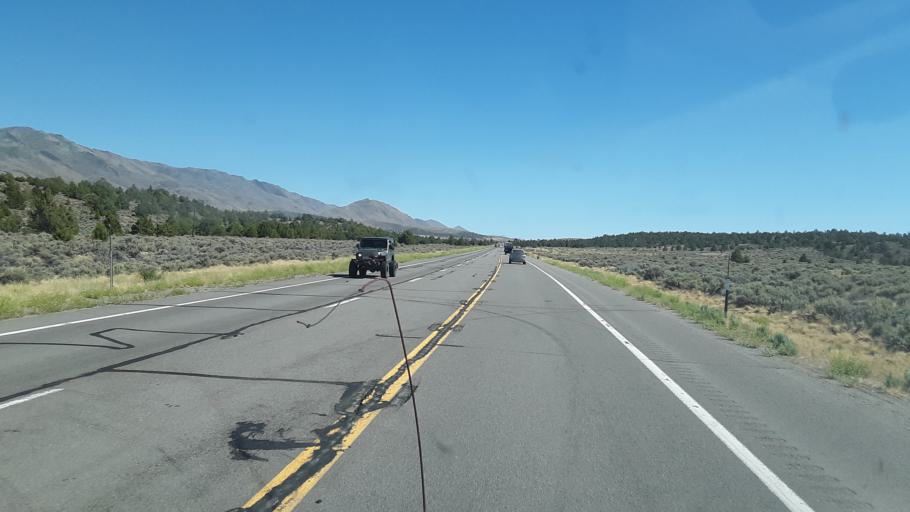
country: US
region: Nevada
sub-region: Washoe County
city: Cold Springs
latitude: 39.8483
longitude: -120.0427
